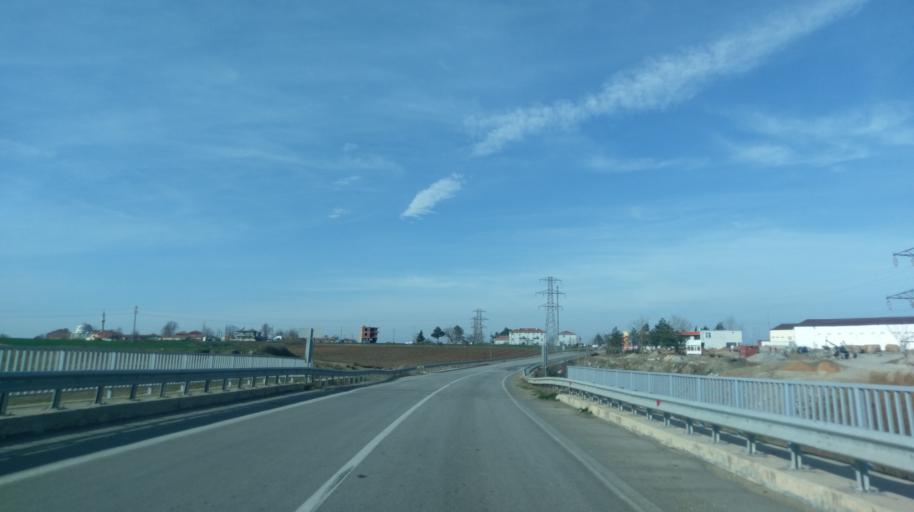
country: TR
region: Edirne
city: Uzun Keupru
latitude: 41.2687
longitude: 26.7121
